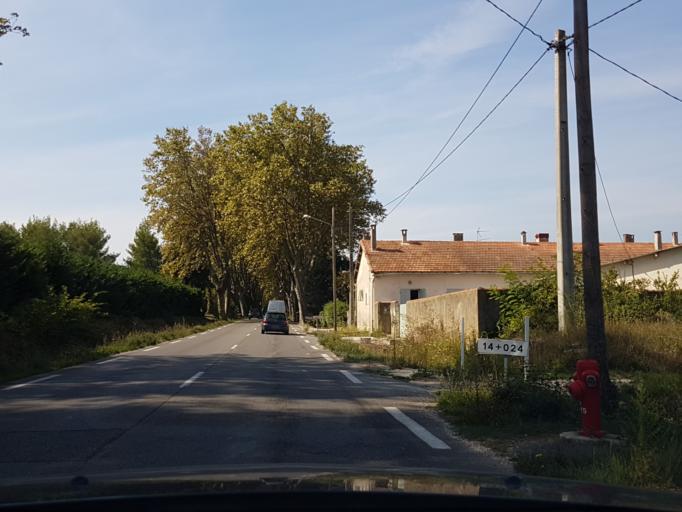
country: FR
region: Provence-Alpes-Cote d'Azur
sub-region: Departement des Bouches-du-Rhone
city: Saint-Remy-de-Provence
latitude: 43.7852
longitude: 4.8668
